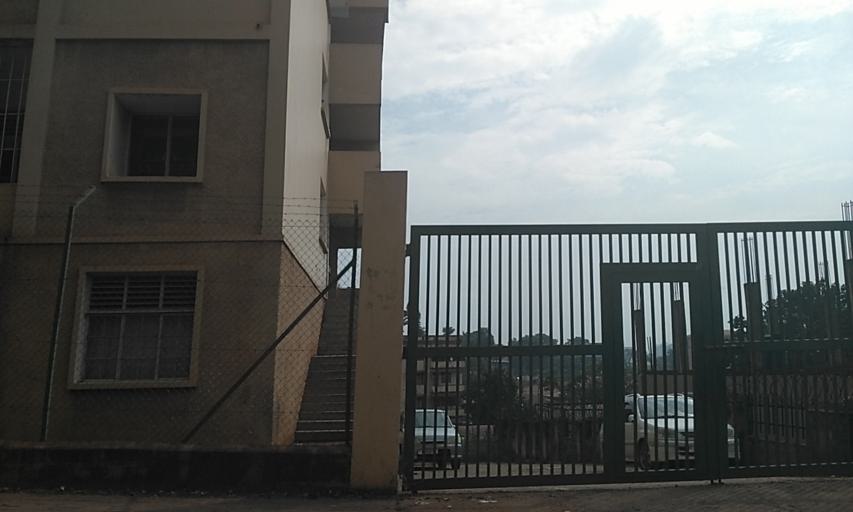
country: UG
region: Central Region
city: Kampala Central Division
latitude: 0.3134
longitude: 32.5652
